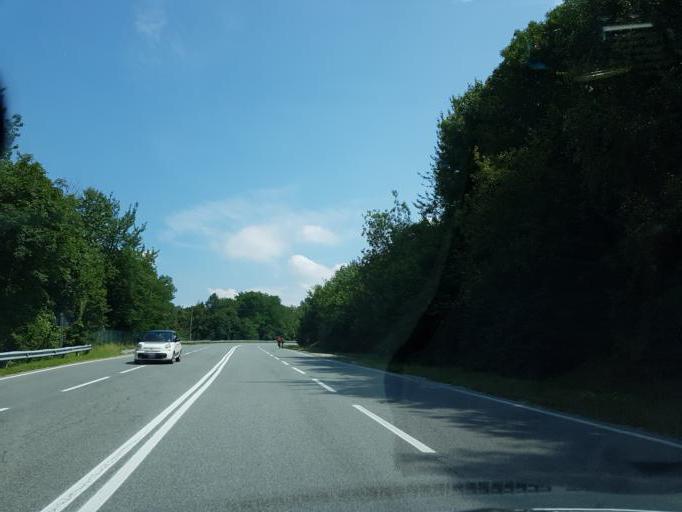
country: IT
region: Piedmont
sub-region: Provincia di Cuneo
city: Vignolo
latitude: 44.3454
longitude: 7.4746
